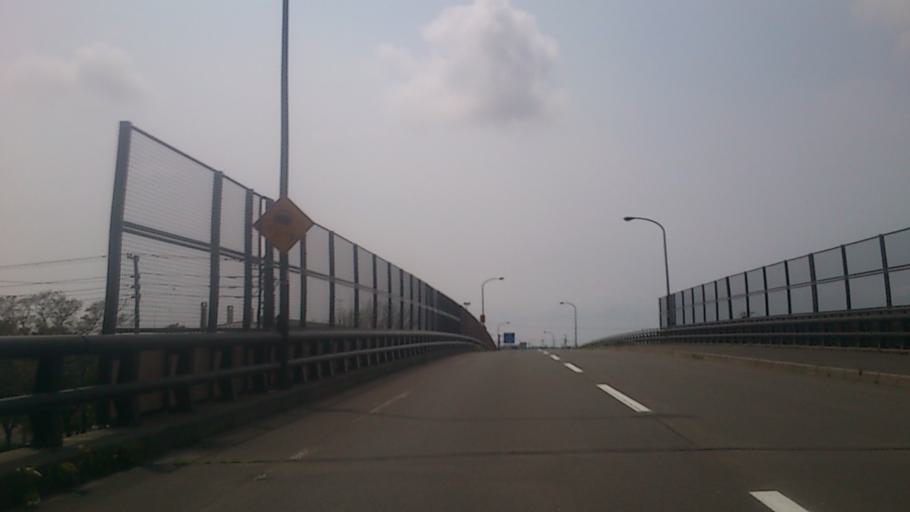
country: JP
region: Hokkaido
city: Nemuro
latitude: 43.2716
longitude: 145.5422
